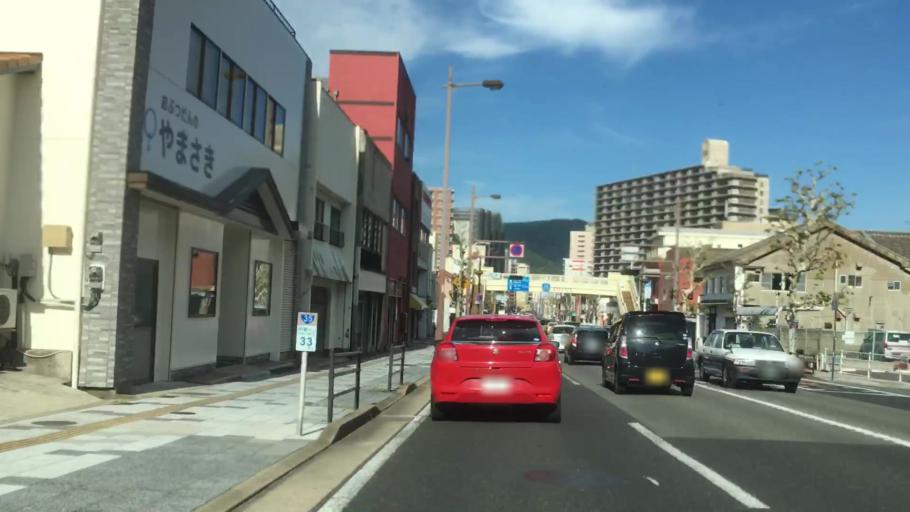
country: JP
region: Nagasaki
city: Sasebo
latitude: 33.1605
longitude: 129.7318
